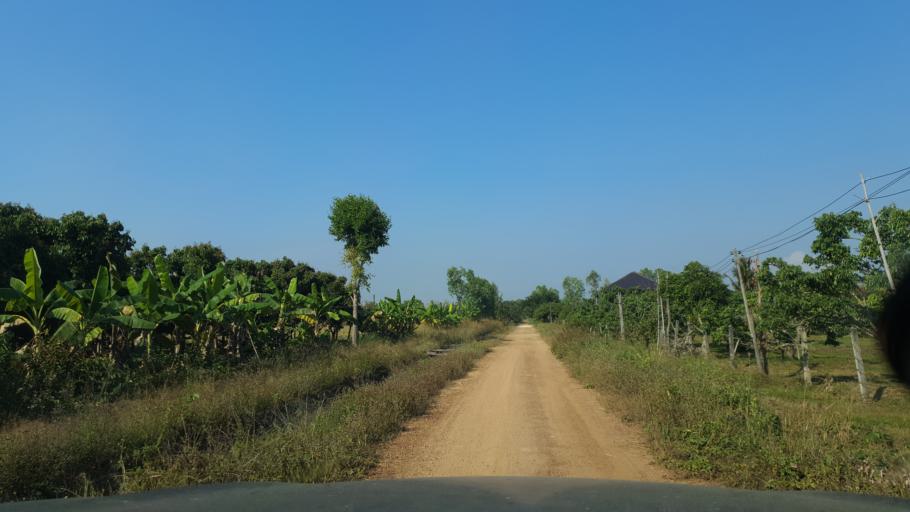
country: TH
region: Lamphun
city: Ban Thi
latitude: 18.6707
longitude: 99.1287
